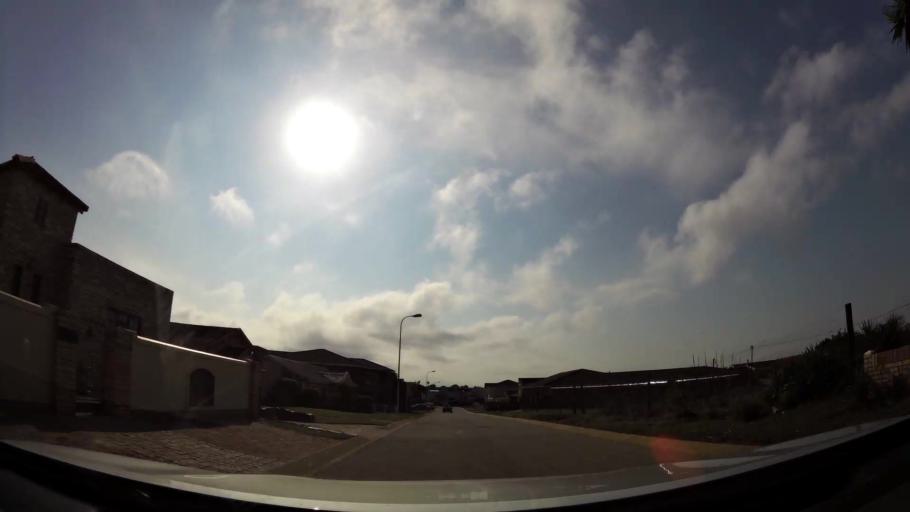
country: ZA
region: Eastern Cape
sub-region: Nelson Mandela Bay Metropolitan Municipality
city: Port Elizabeth
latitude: -33.9248
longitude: 25.5300
